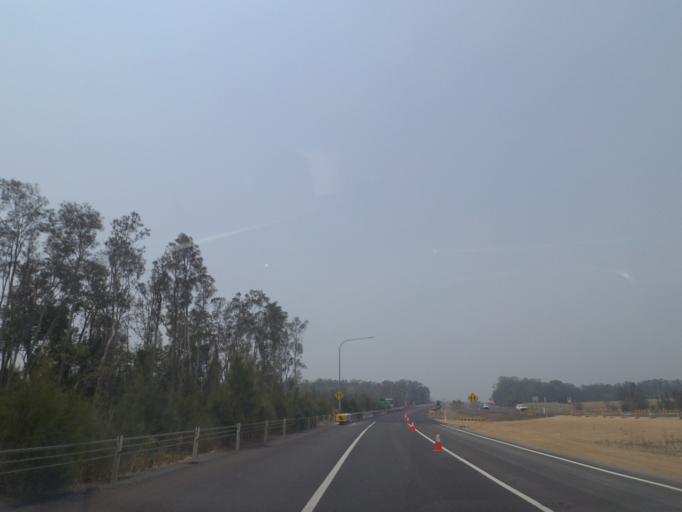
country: AU
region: New South Wales
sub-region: Ballina
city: Ballina
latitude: -28.8672
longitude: 153.4945
